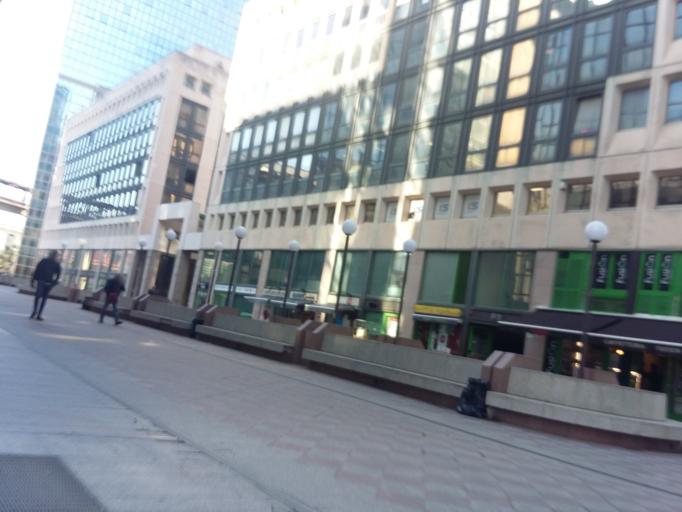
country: IT
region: Campania
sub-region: Provincia di Napoli
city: Napoli
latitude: 40.8575
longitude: 14.2801
